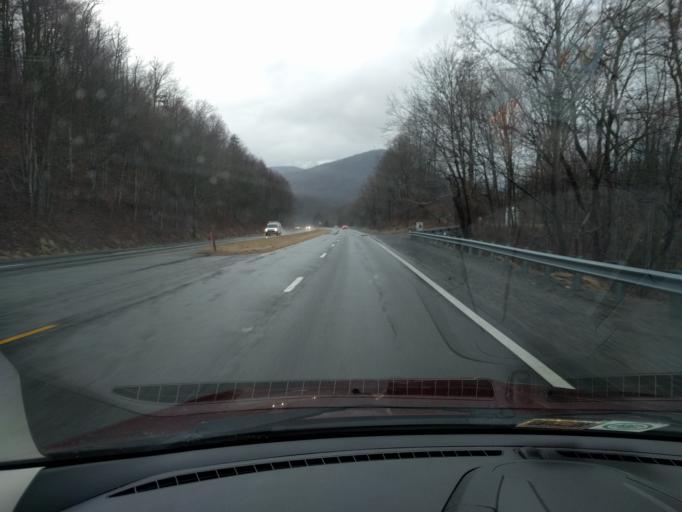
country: US
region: Virginia
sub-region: Montgomery County
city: Prices Fork
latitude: 37.2868
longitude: -80.4843
